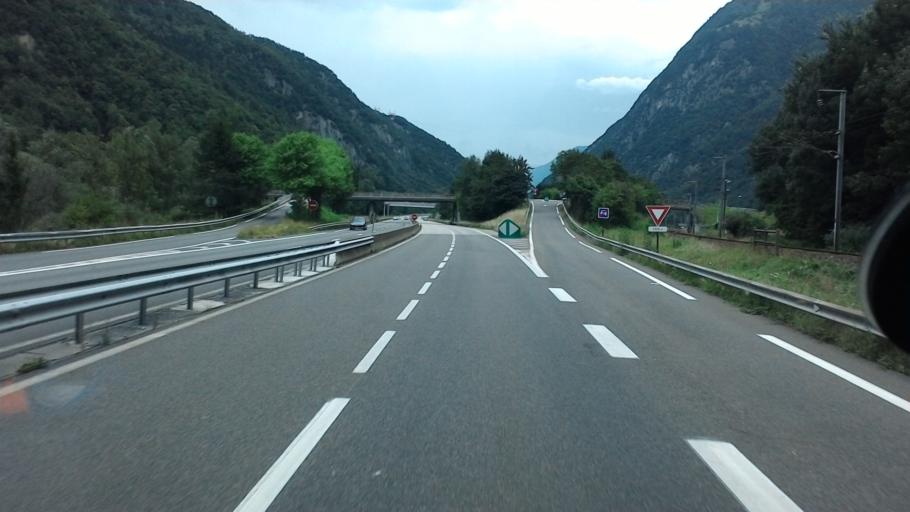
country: FR
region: Rhone-Alpes
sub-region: Departement de la Savoie
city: Aigueblanche
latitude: 45.5532
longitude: 6.4689
